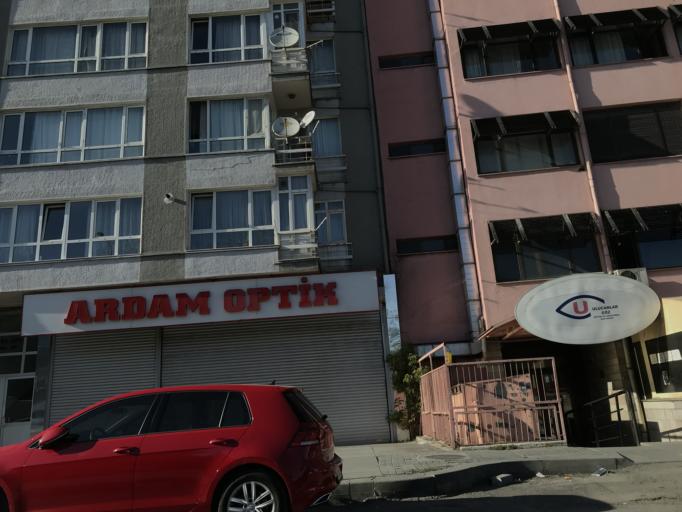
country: TR
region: Ankara
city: Cankaya
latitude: 39.9372
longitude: 32.8700
